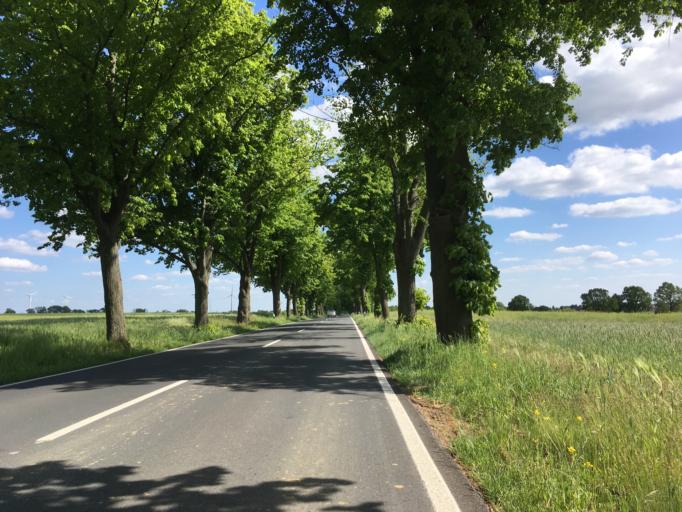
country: DE
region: Brandenburg
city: Ahrensfelde
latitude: 52.6162
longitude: 13.6145
